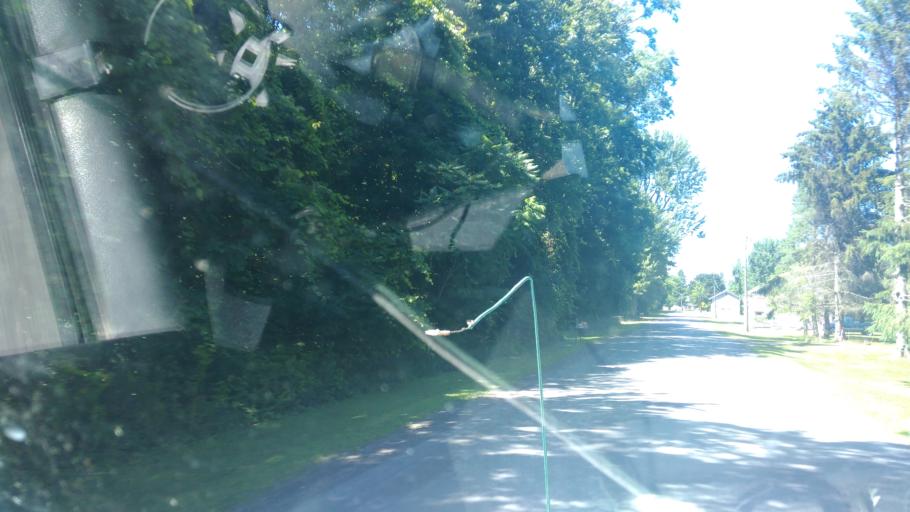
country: US
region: New York
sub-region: Wayne County
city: Sodus
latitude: 43.1822
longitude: -76.9794
